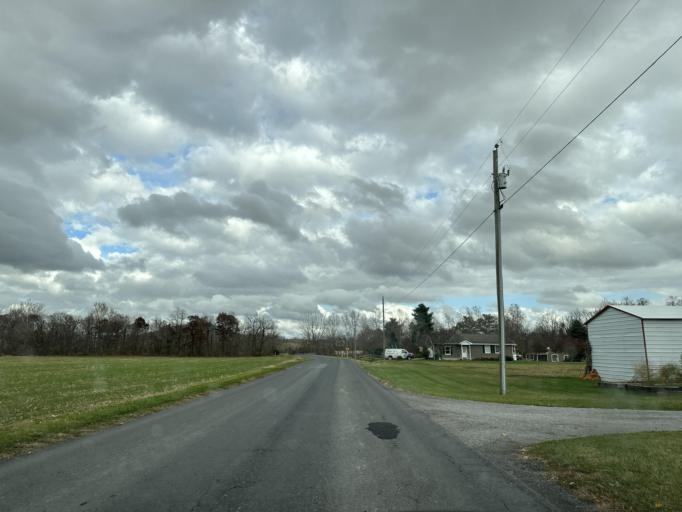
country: US
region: Virginia
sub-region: Rockingham County
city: Bridgewater
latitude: 38.4330
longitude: -78.9880
